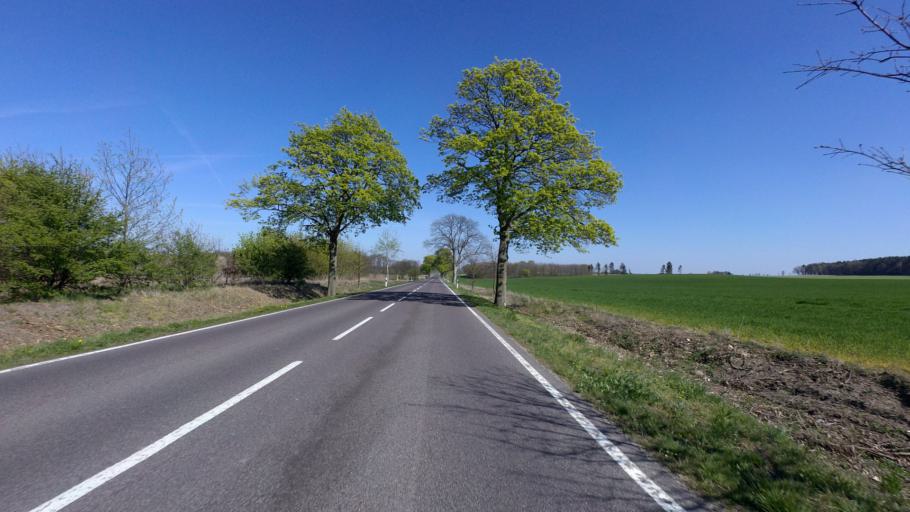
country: DE
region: Saxony-Anhalt
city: Kalbe
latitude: 52.6488
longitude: 11.3082
